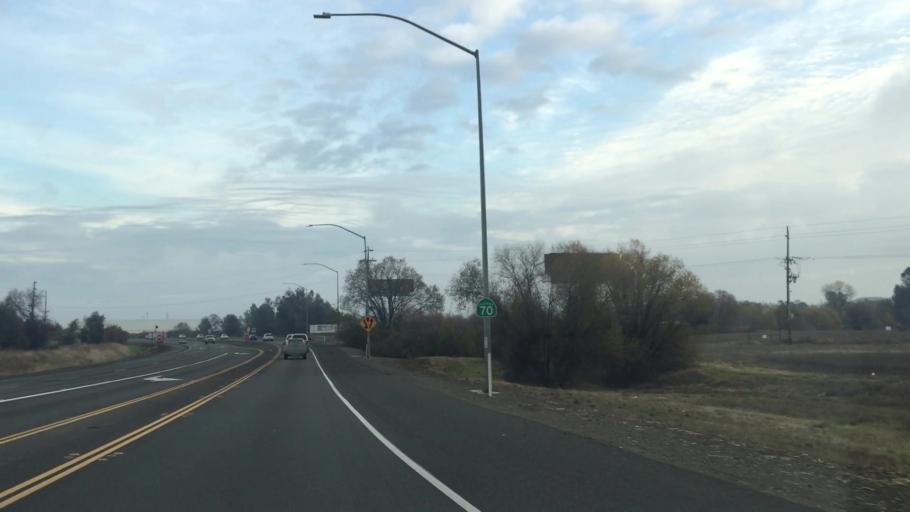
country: US
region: California
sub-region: Butte County
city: South Oroville
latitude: 39.4645
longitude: -121.5784
